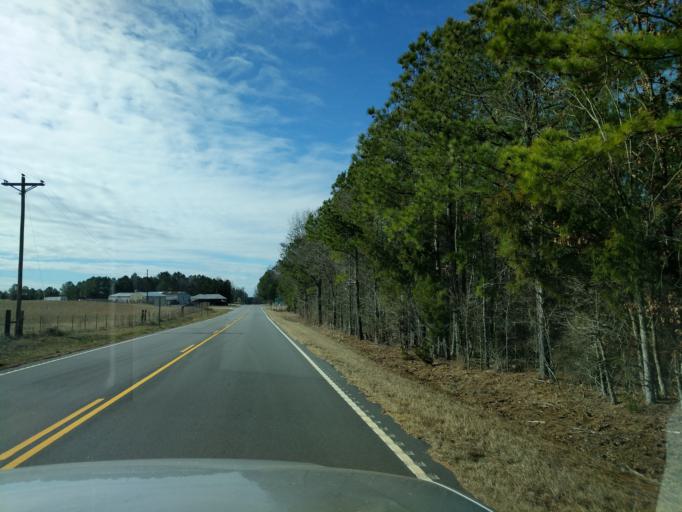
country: US
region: South Carolina
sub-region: Edgefield County
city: Edgefield
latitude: 33.9434
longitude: -81.9252
